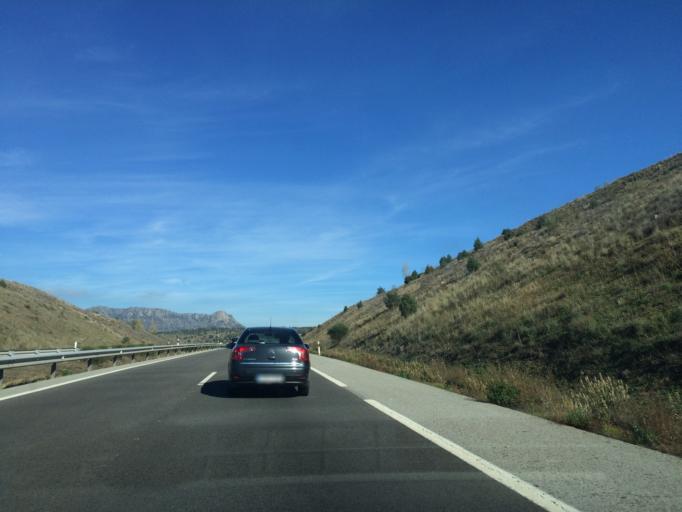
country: ES
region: Madrid
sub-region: Provincia de Madrid
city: Cabanillas de la Sierra
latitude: 40.8184
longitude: -3.6156
